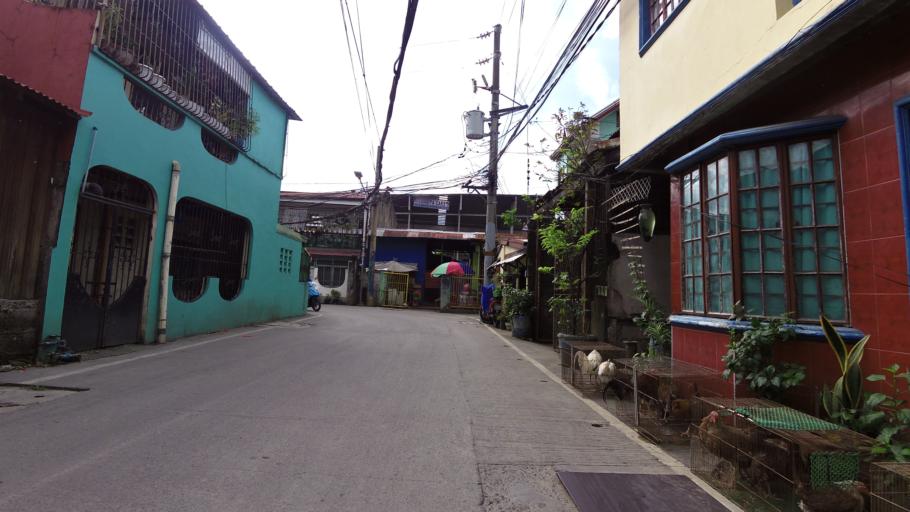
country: PH
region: Calabarzon
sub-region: Province of Rizal
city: Cainta
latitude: 14.5724
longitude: 121.1122
